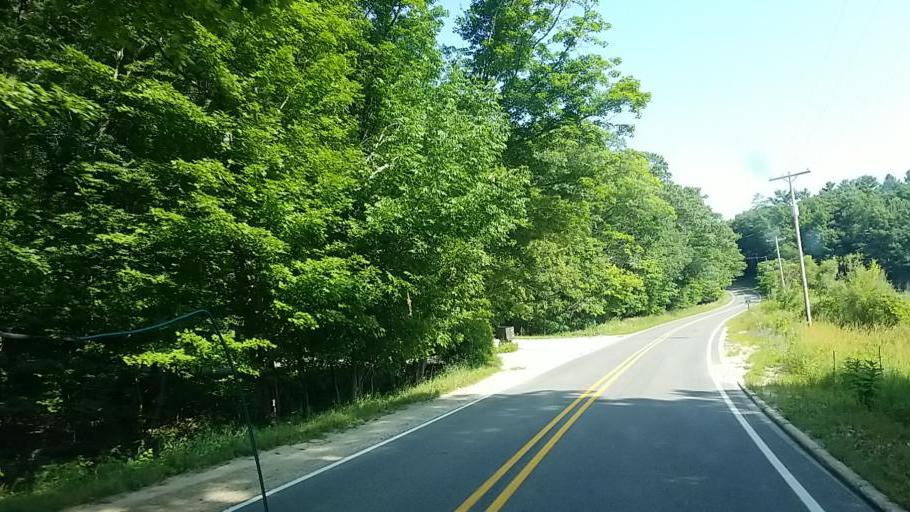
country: US
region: Michigan
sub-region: Muskegon County
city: Whitehall
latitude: 43.3277
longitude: -86.3995
